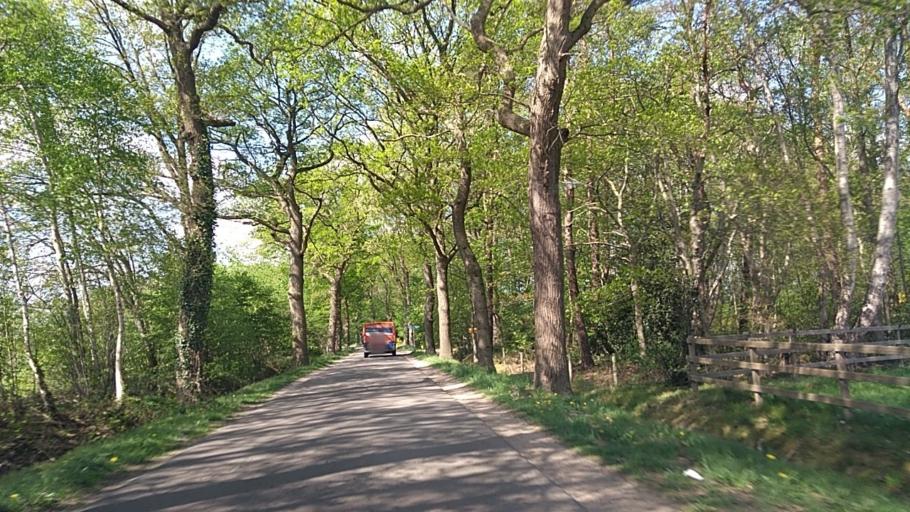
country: NL
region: Overijssel
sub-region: Gemeente Haaksbergen
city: Haaksbergen
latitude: 52.1395
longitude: 6.7130
